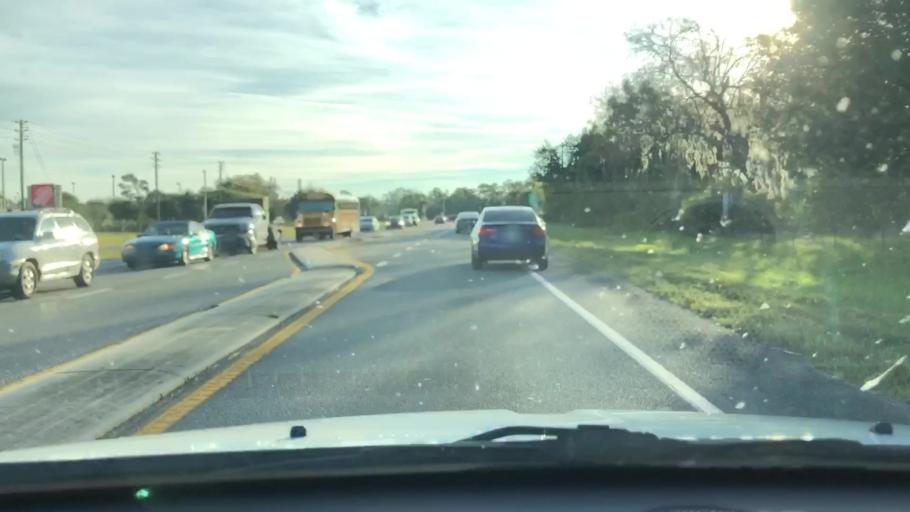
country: US
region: Florida
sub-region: Osceola County
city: Campbell
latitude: 28.2553
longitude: -81.4843
